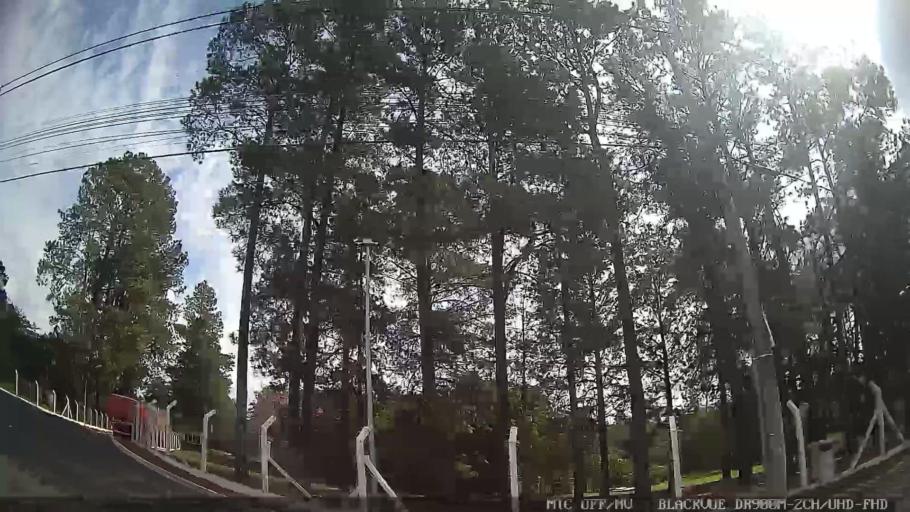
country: BR
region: Sao Paulo
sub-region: Indaiatuba
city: Indaiatuba
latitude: -23.1432
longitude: -47.2495
